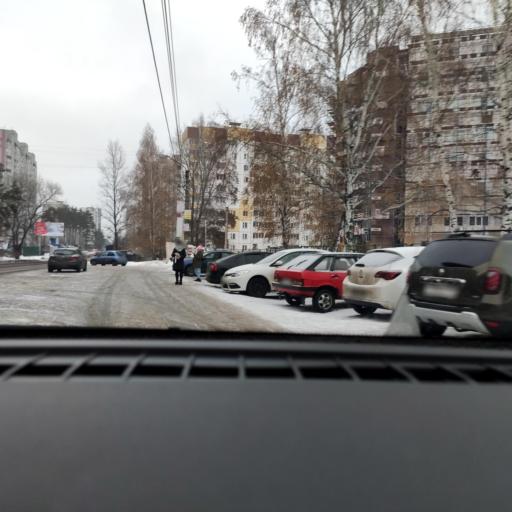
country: RU
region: Voronezj
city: Voronezh
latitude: 51.6861
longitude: 39.2786
